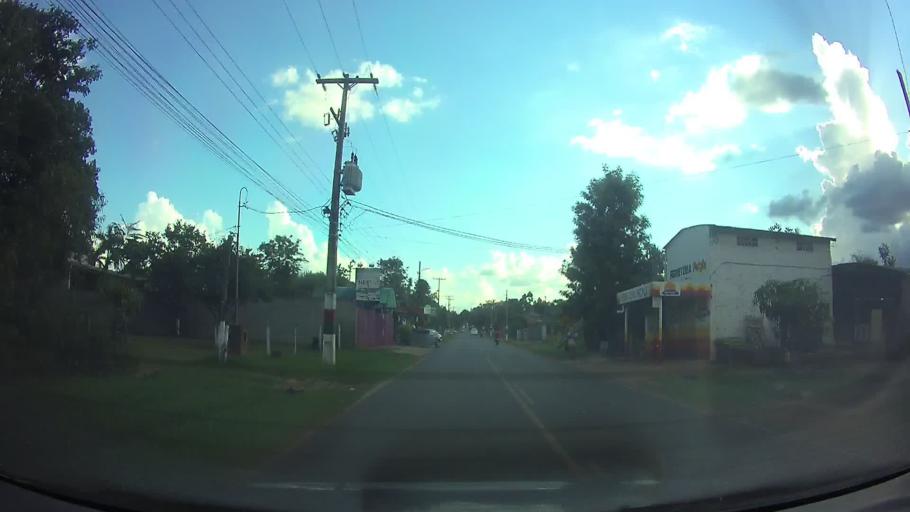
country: PY
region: Central
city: Aregua
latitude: -25.2751
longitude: -57.4300
